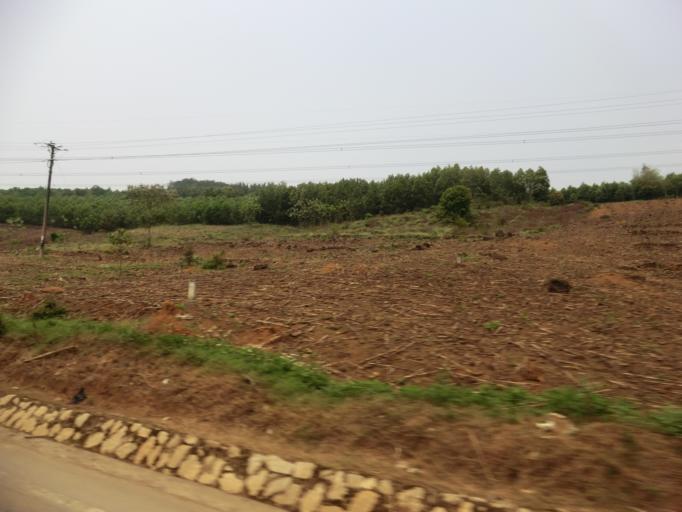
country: VN
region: Thanh Hoa
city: Thi Tran Cam Thuy
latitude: 20.1615
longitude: 105.4690
